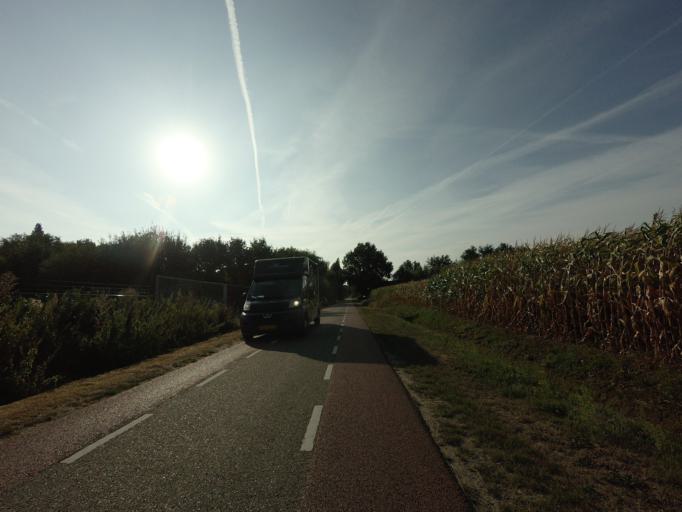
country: NL
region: North Brabant
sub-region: Gemeente Landerd
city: Zeeland
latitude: 51.6832
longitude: 5.6933
